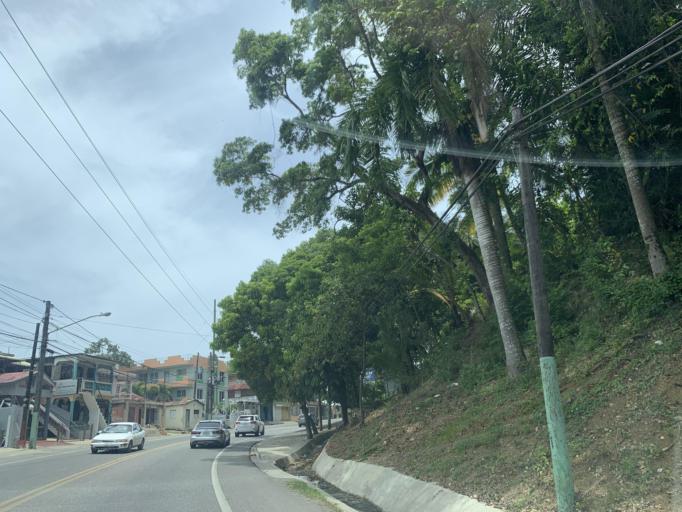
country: DO
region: Puerto Plata
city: Cabarete
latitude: 19.7512
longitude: -70.5206
